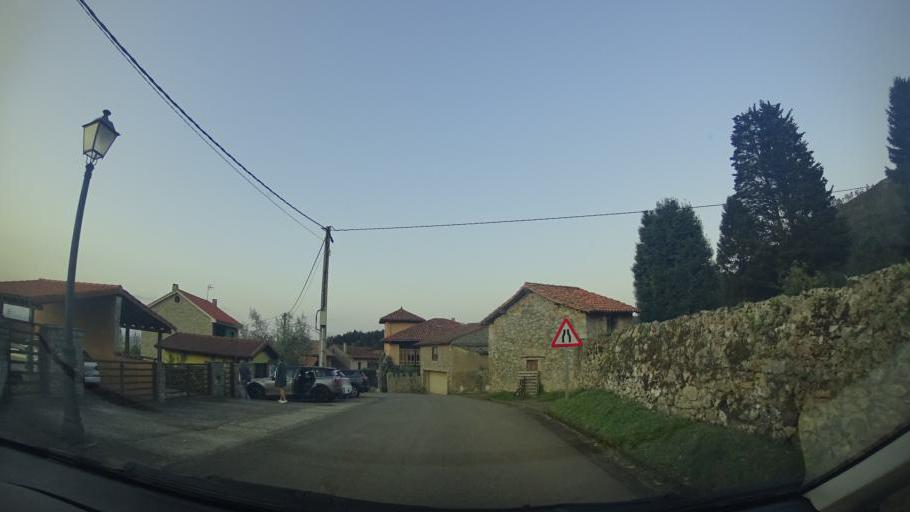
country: ES
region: Asturias
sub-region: Province of Asturias
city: Colunga
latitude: 43.4574
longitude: -5.2055
